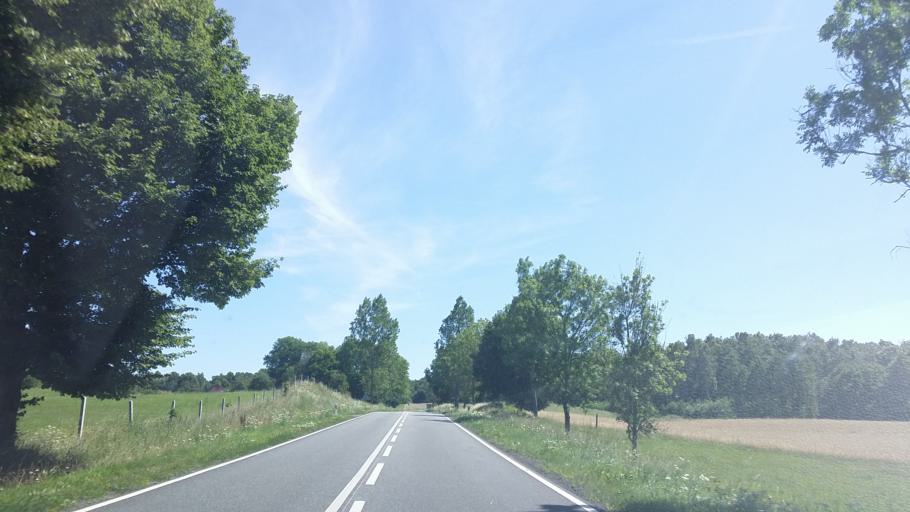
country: PL
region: West Pomeranian Voivodeship
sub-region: Powiat lobeski
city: Wegorzyno
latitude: 53.4946
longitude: 15.5757
